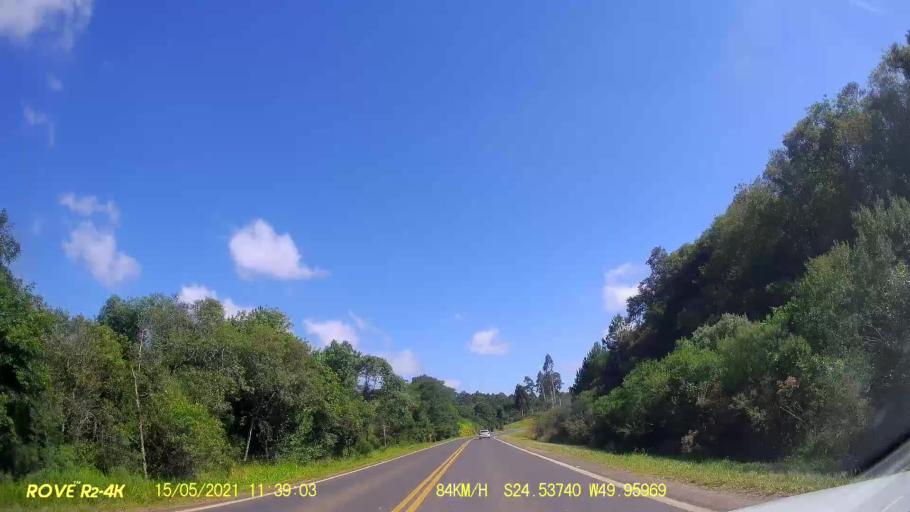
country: BR
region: Parana
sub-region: Pirai Do Sul
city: Pirai do Sul
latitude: -24.5369
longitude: -49.9596
